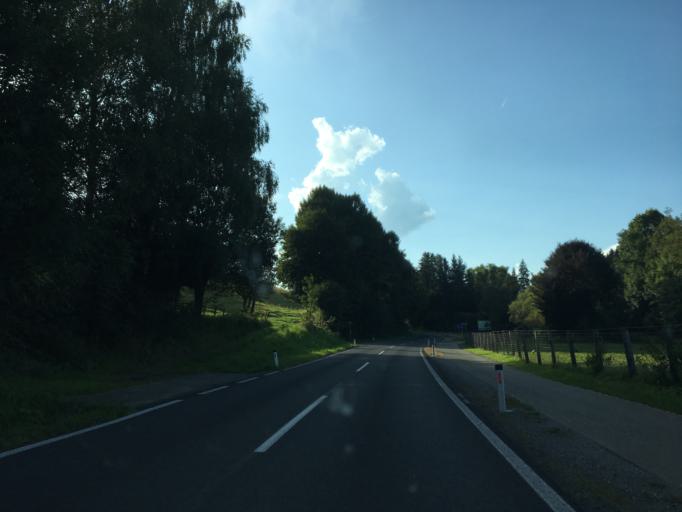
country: AT
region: Styria
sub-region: Politischer Bezirk Murau
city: Neumarkt in Steiermark
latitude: 47.0807
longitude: 14.4176
